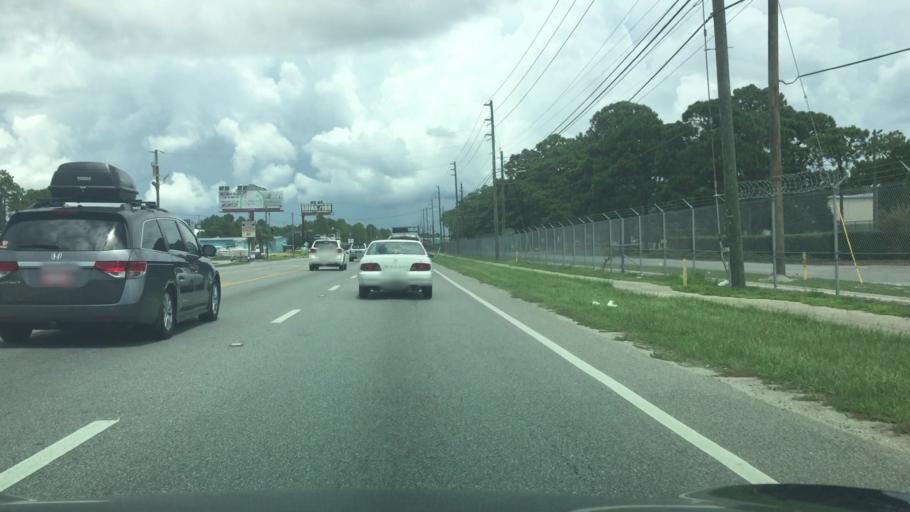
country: US
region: Florida
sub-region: Bay County
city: Upper Grand Lagoon
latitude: 30.1794
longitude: -85.7605
